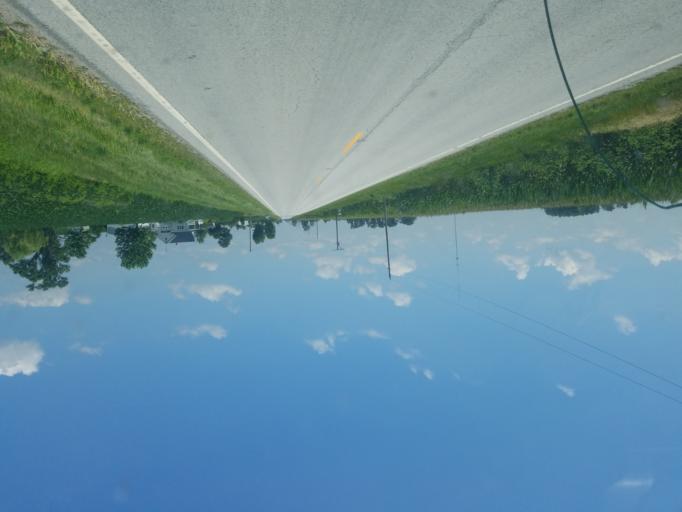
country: US
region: Ohio
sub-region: Allen County
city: Spencerville
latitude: 40.7141
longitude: -84.3729
